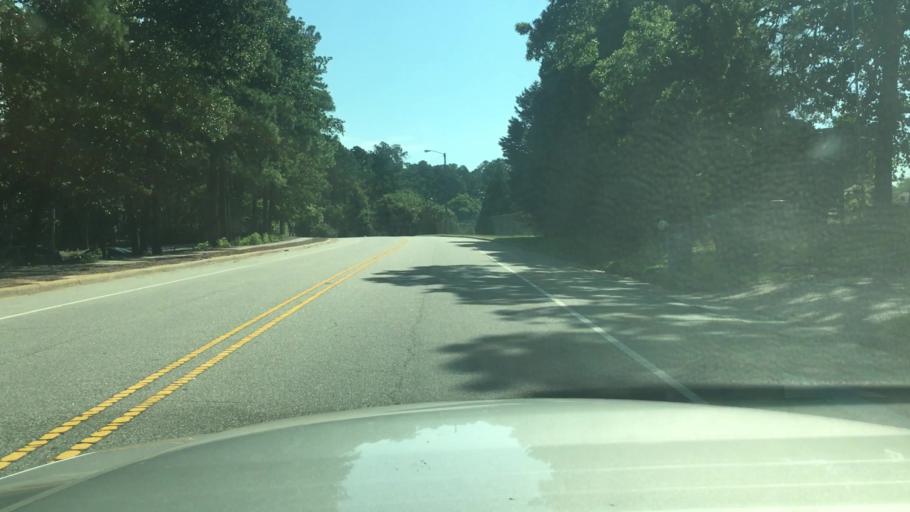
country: US
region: North Carolina
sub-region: Cumberland County
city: Fayetteville
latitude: 35.1122
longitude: -78.9081
